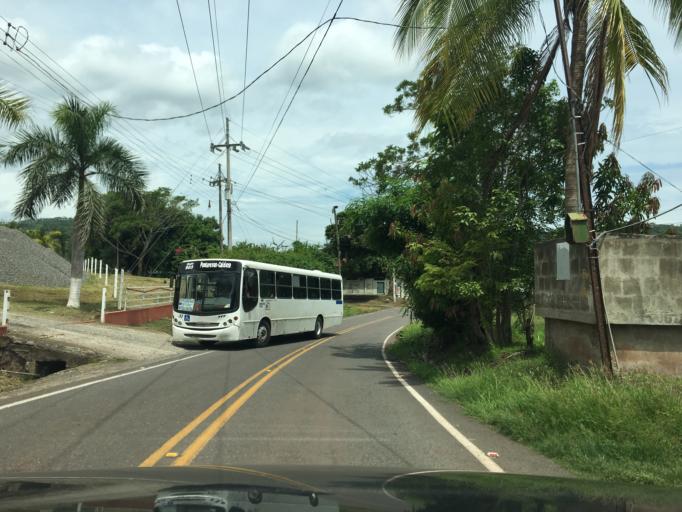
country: CR
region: Puntarenas
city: Esparza
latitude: 9.9308
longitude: -84.6925
